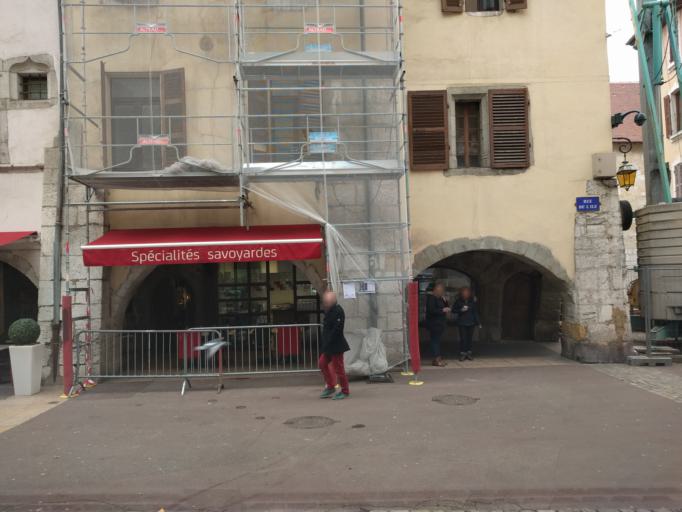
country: FR
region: Rhone-Alpes
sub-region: Departement de la Haute-Savoie
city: Annecy
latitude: 45.8982
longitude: 6.1267
